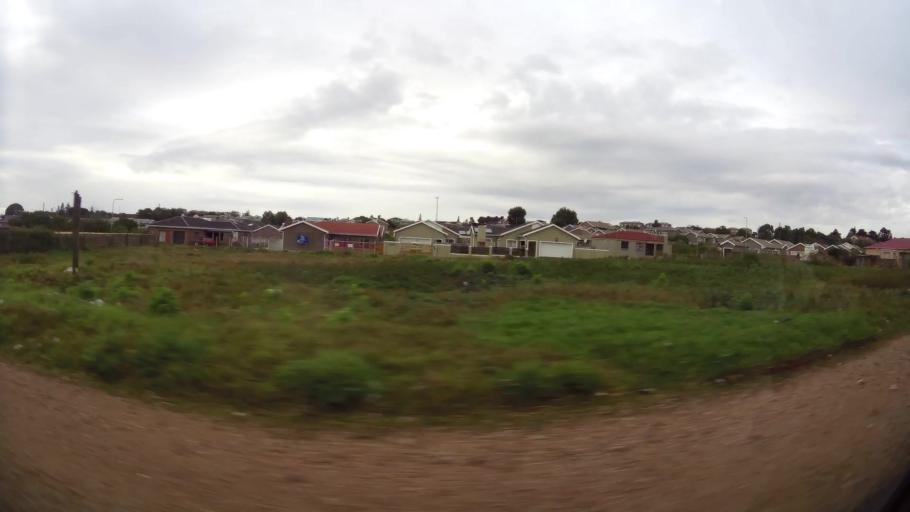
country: ZA
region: Eastern Cape
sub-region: Nelson Mandela Bay Metropolitan Municipality
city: Port Elizabeth
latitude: -33.9938
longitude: 25.5404
